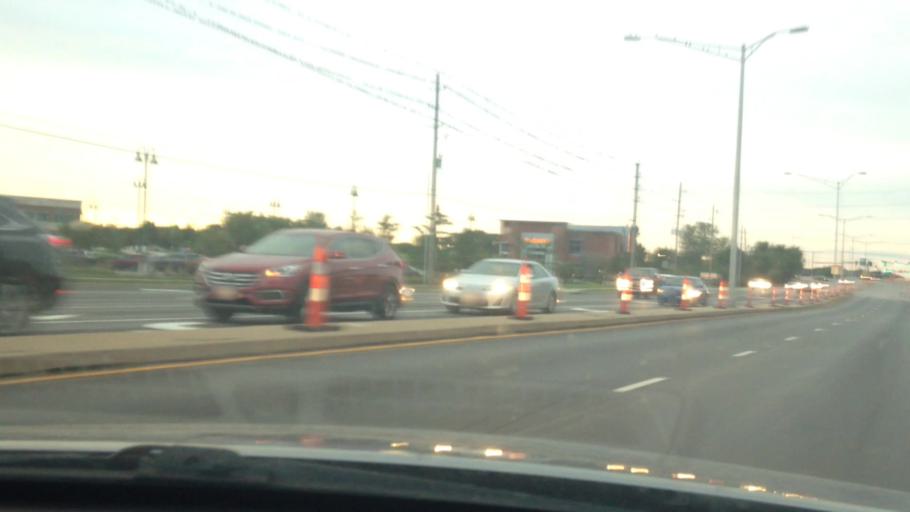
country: US
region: Missouri
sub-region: Jackson County
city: Lees Summit
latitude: 38.9408
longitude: -94.3782
